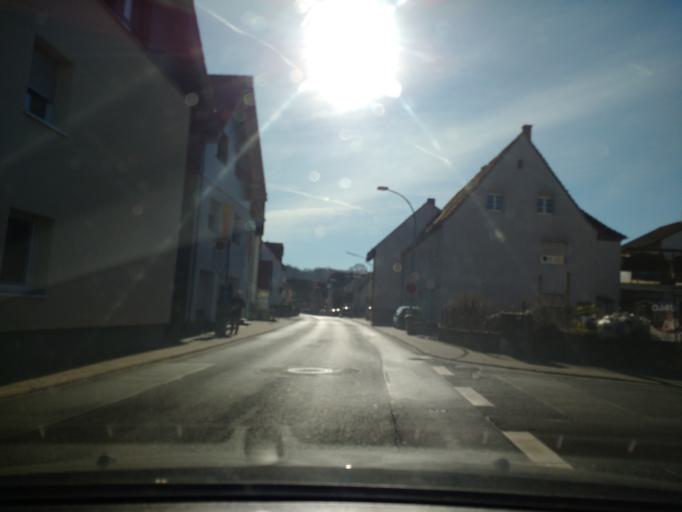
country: DE
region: Bavaria
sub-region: Regierungsbezirk Unterfranken
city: Geiselbach
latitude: 50.1407
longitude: 9.1432
